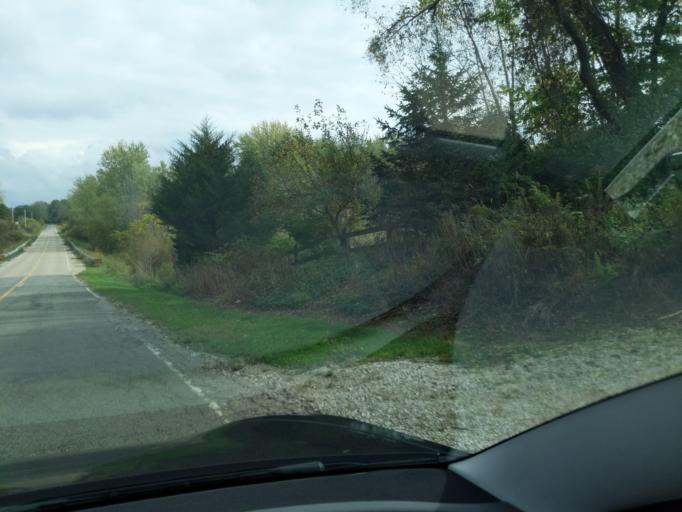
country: US
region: Michigan
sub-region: Ingham County
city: Leslie
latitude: 42.4115
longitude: -84.4754
